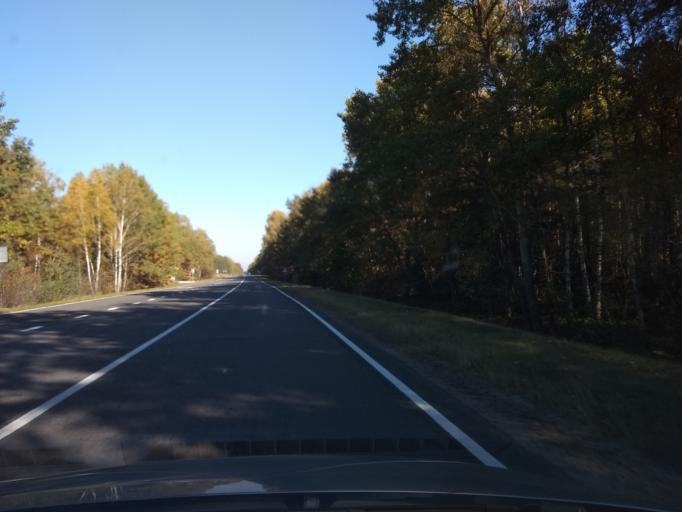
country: BY
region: Brest
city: Kobryn
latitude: 52.0344
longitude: 24.2704
